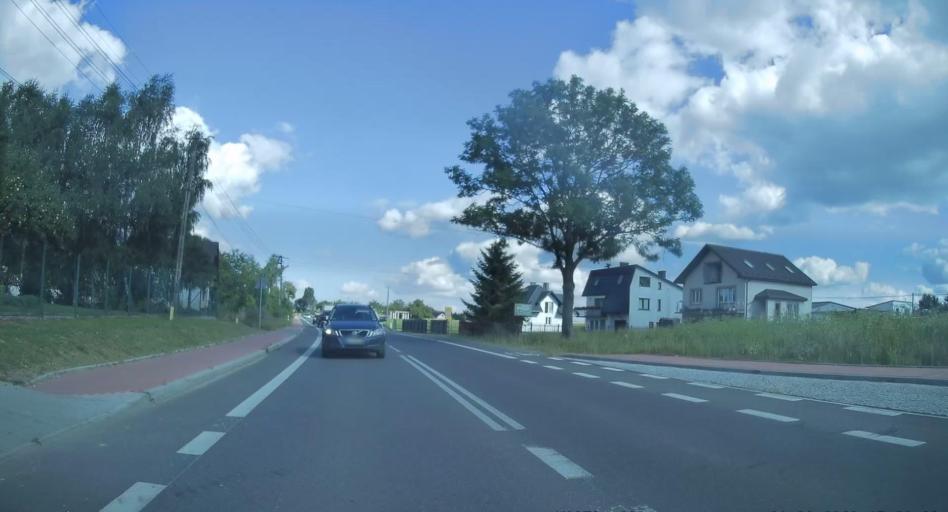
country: PL
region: Swietokrzyskie
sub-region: Powiat kielecki
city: Bodzentyn
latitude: 50.9318
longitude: 20.9731
